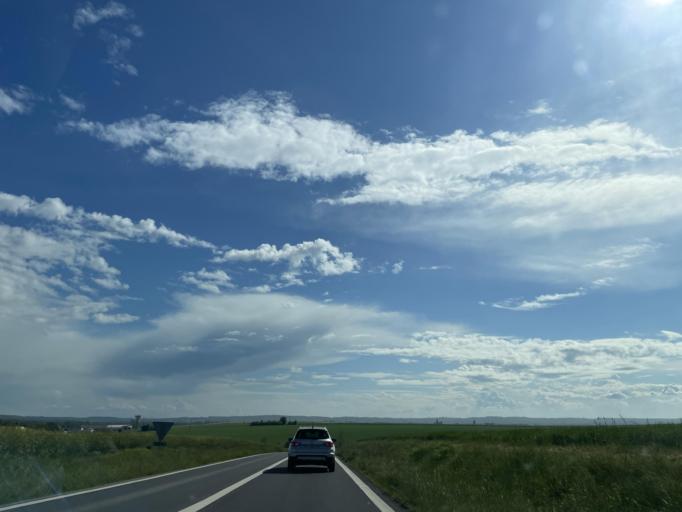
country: FR
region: Ile-de-France
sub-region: Departement de Seine-et-Marne
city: Charny
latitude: 48.9530
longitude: 2.7763
